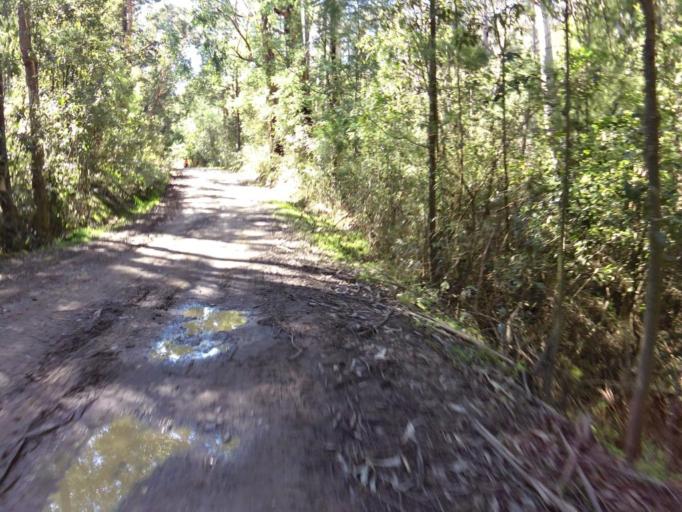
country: AU
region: Victoria
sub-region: Baw Baw
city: Warragul
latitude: -38.0683
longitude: 145.9310
